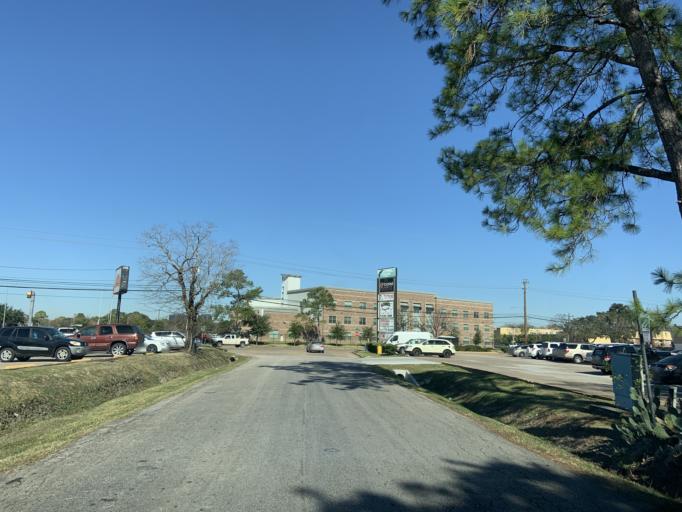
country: US
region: Texas
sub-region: Harris County
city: Bellaire
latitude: 29.6839
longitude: -95.5130
